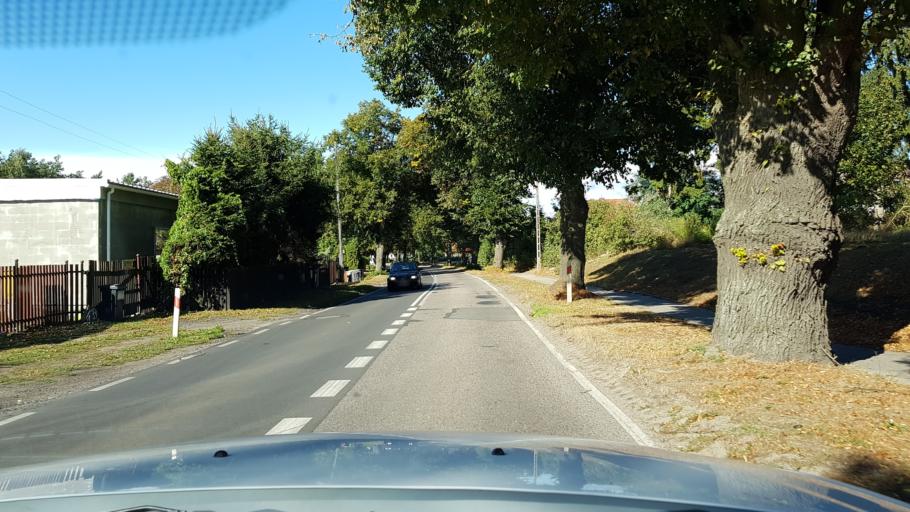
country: PL
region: West Pomeranian Voivodeship
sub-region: Powiat gryfinski
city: Gryfino
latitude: 53.2098
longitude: 14.5007
